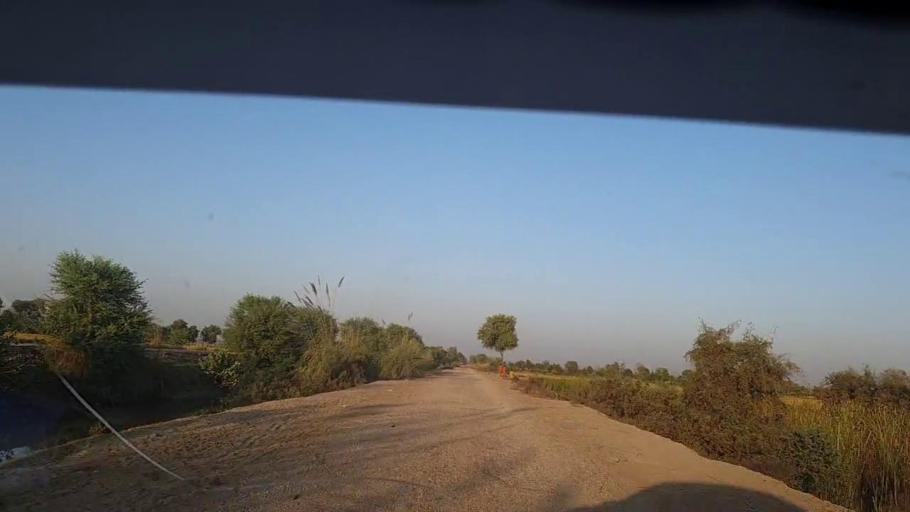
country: PK
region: Sindh
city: Ratodero
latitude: 27.8857
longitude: 68.2128
